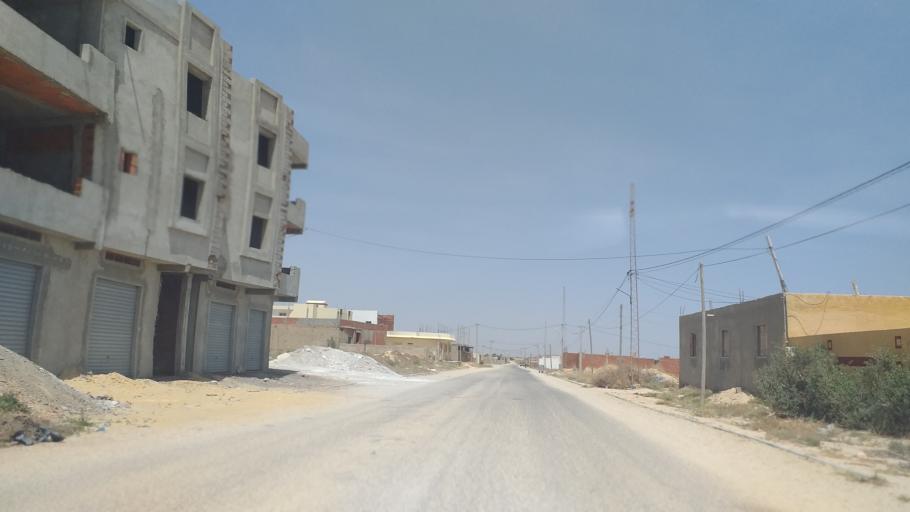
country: TN
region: Qabis
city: Gabes
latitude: 33.9540
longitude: 10.0665
